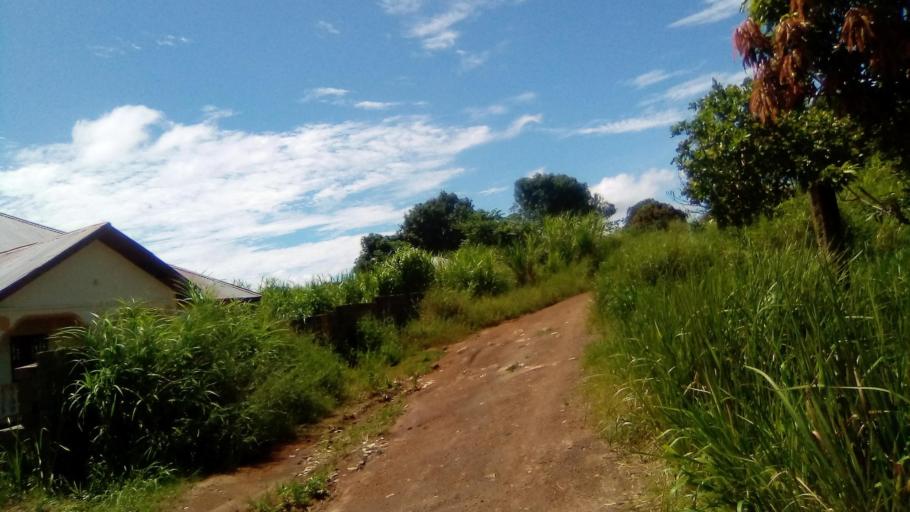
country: SL
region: Eastern Province
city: Simbakoro
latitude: 8.6313
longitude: -10.9988
